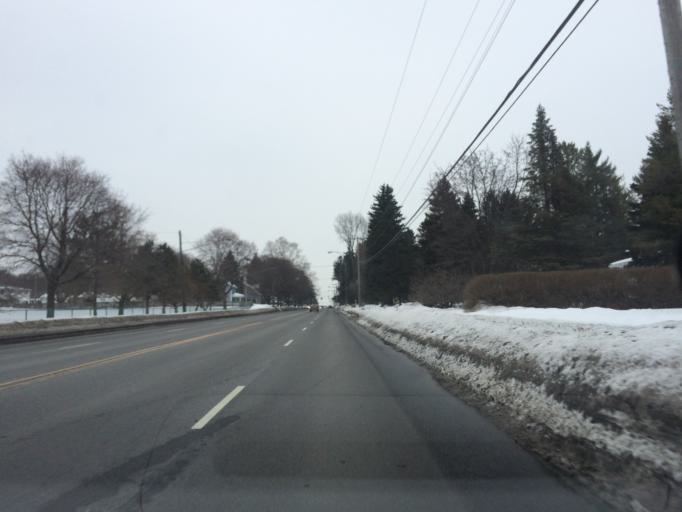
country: US
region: New York
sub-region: Monroe County
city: East Rochester
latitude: 43.1061
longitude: -77.4930
